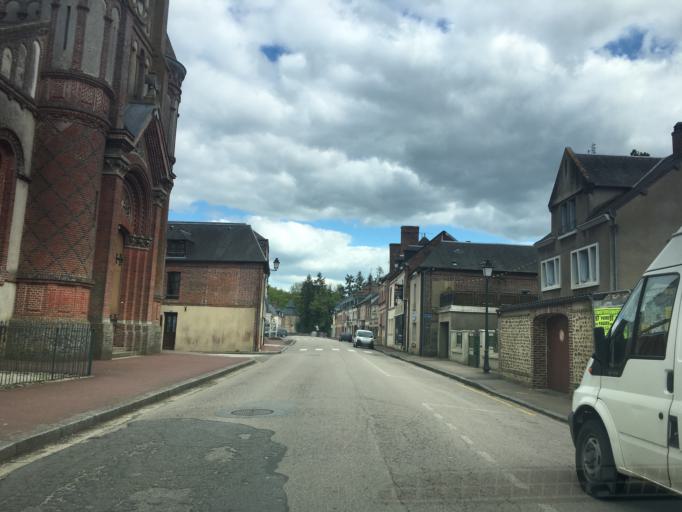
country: FR
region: Lower Normandy
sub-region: Departement de l'Orne
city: Aube-sur-Rile
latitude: 48.8413
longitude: 0.5098
